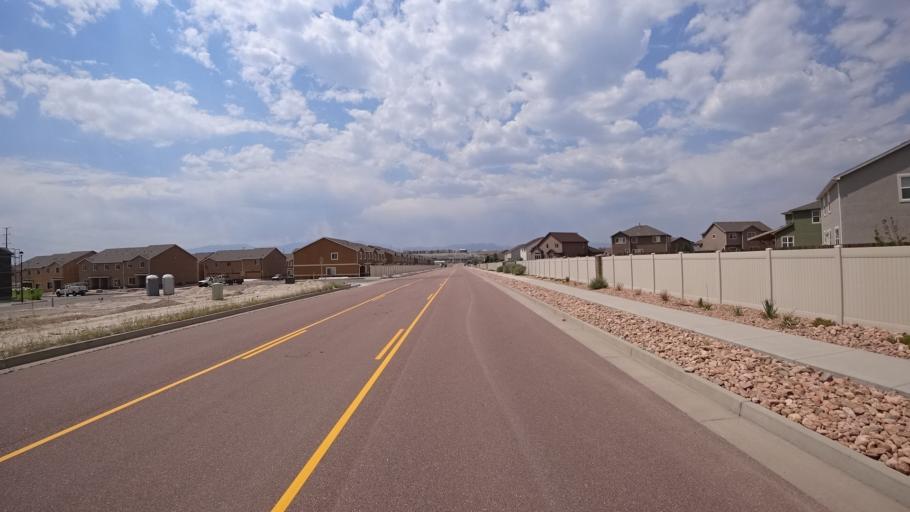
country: US
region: Colorado
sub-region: El Paso County
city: Black Forest
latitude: 38.9437
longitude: -104.6898
